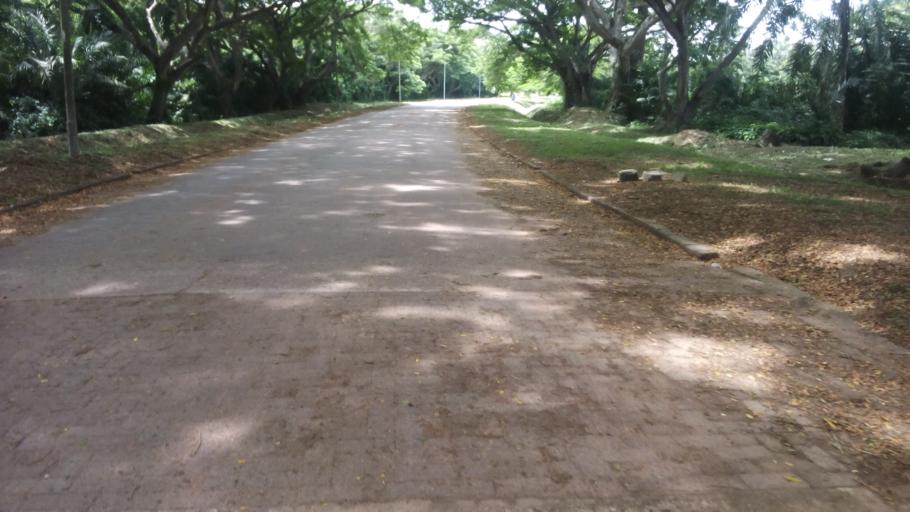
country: GH
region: Central
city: Cape Coast
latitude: 5.1263
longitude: -1.2891
